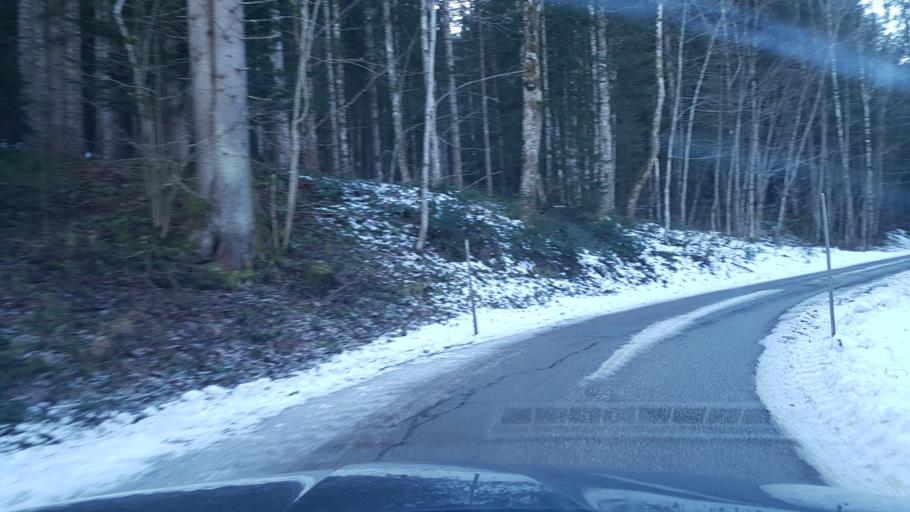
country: AT
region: Salzburg
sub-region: Politischer Bezirk Hallein
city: Abtenau
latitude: 47.5771
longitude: 13.4245
